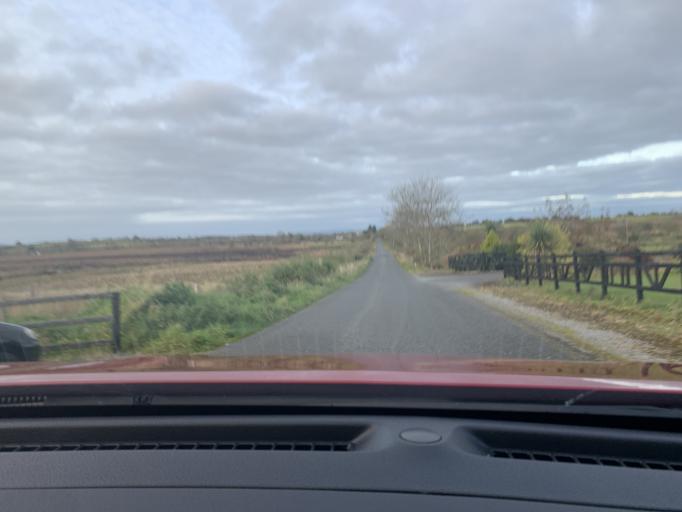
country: IE
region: Connaught
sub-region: Roscommon
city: Ballaghaderreen
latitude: 53.9931
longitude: -8.6098
